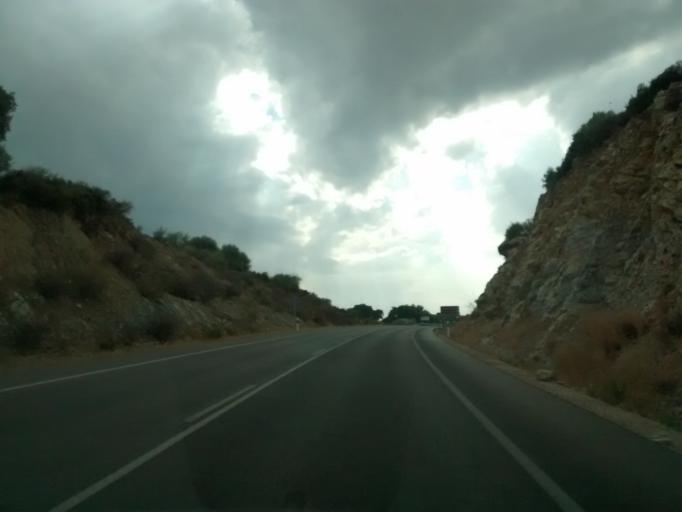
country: ES
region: Andalusia
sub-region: Provincia de Cadiz
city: Algar
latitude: 36.7435
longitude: -5.6345
